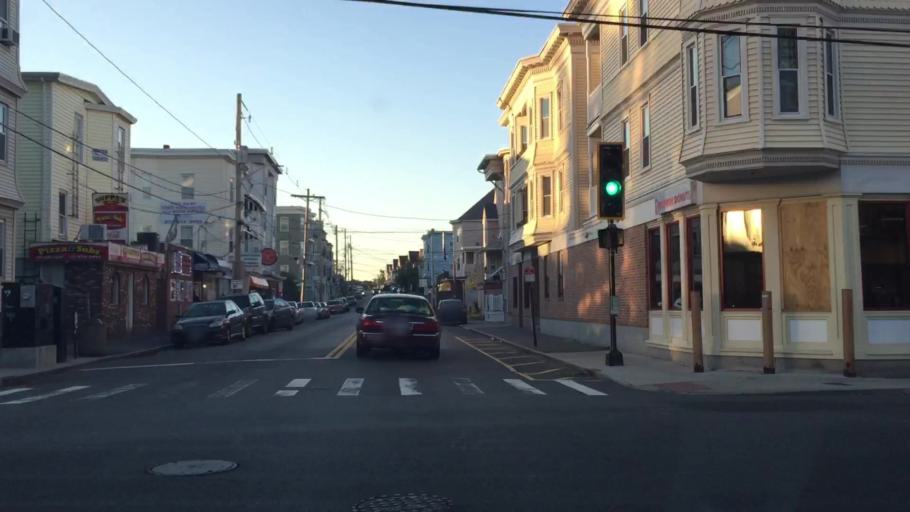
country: US
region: Massachusetts
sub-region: Middlesex County
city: Lowell
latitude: 42.6537
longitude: -71.3267
